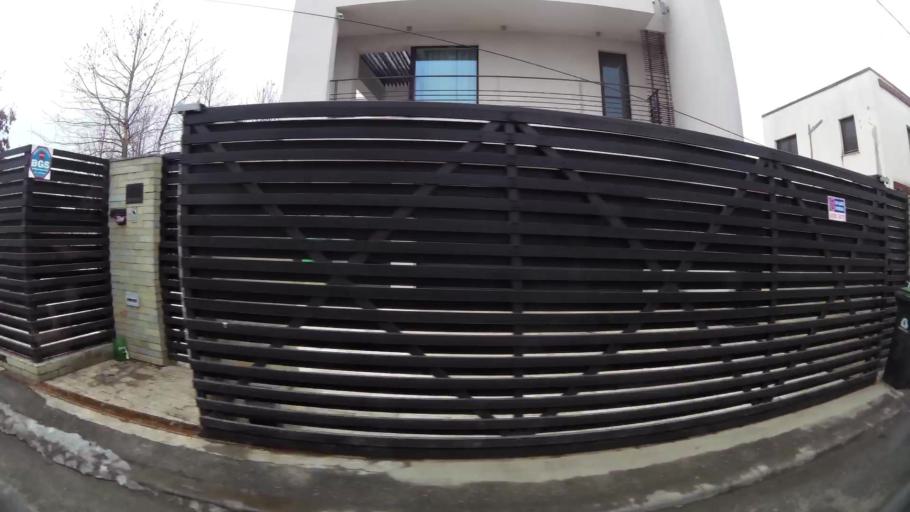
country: RO
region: Ilfov
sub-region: Comuna Otopeni
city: Otopeni
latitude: 44.5532
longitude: 26.0965
